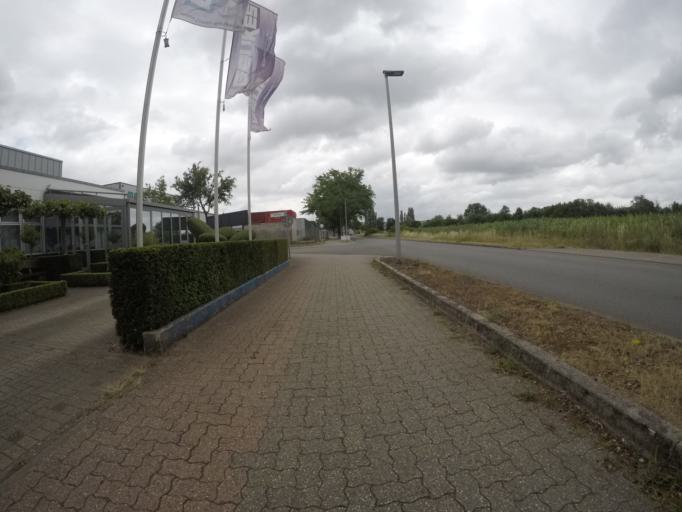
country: DE
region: North Rhine-Westphalia
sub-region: Regierungsbezirk Dusseldorf
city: Bocholt
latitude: 51.8072
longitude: 6.6046
